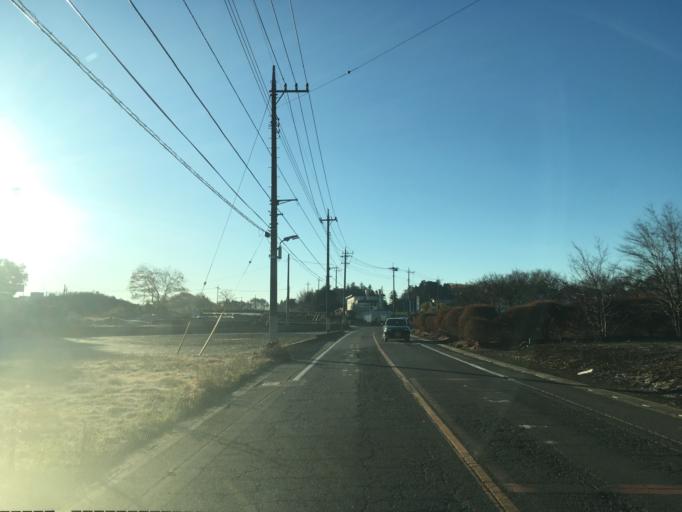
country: JP
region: Saitama
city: Tokorozawa
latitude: 35.7959
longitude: 139.4158
